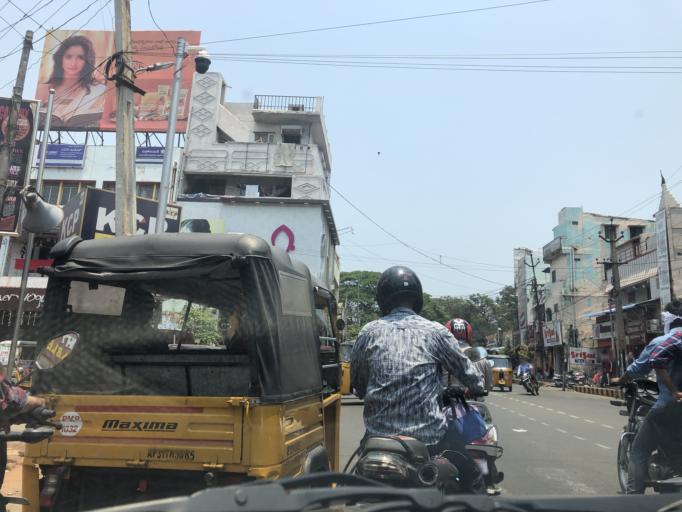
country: IN
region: Andhra Pradesh
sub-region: Vishakhapatnam
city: Yarada
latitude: 17.7138
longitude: 83.3035
